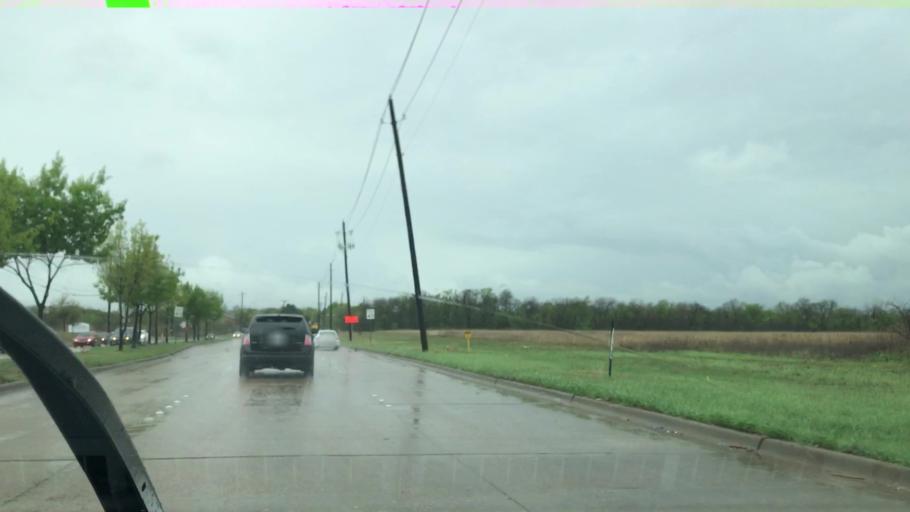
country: US
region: Texas
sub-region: Denton County
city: The Colony
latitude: 33.0443
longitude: -96.8813
